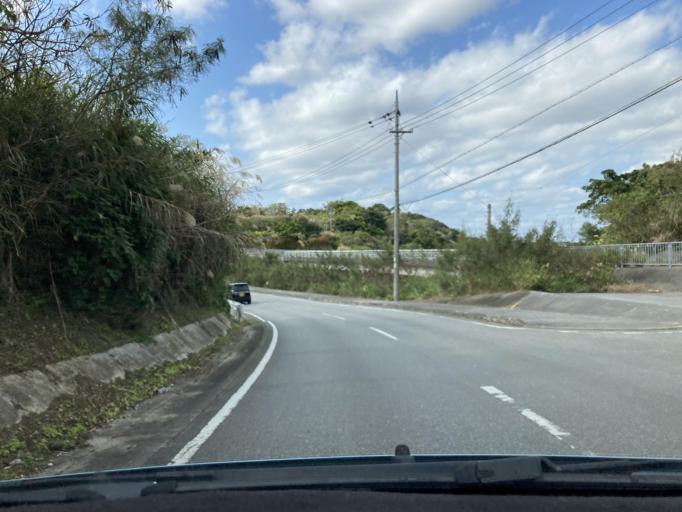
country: JP
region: Okinawa
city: Tomigusuku
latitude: 26.1698
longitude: 127.7640
